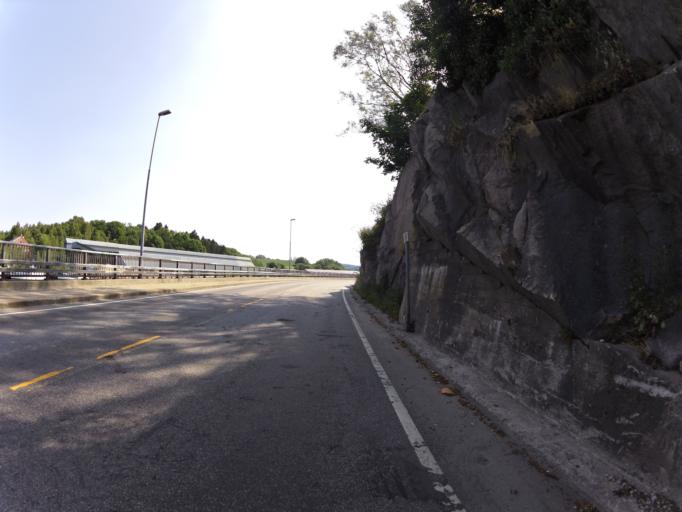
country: NO
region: Ostfold
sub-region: Sarpsborg
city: Sarpsborg
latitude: 59.2701
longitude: 11.0893
